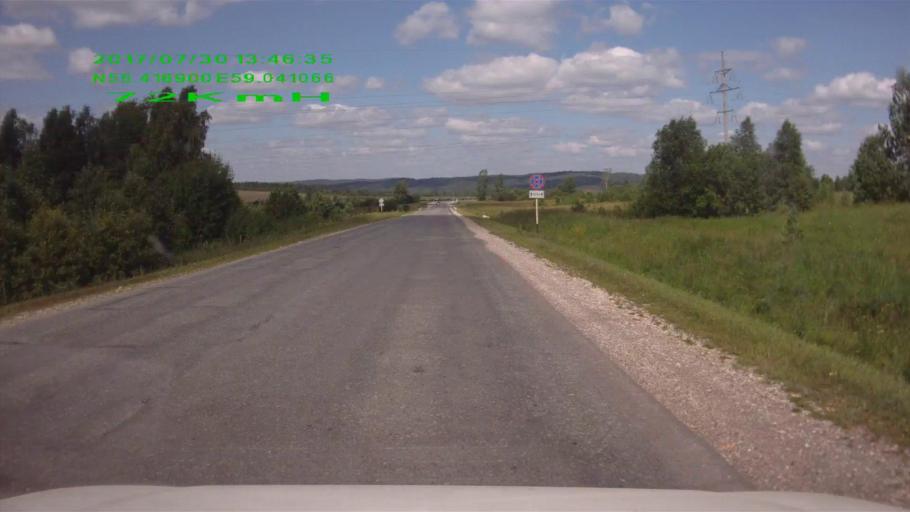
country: RU
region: Sverdlovsk
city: Mikhaylovsk
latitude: 56.4172
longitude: 59.0411
